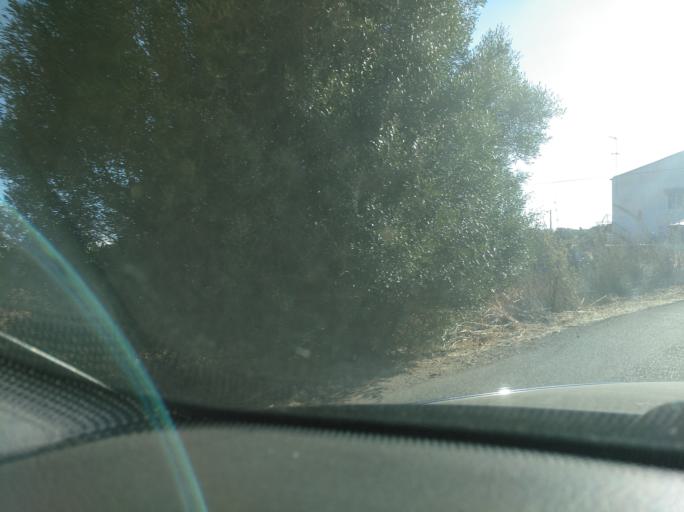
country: PT
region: Faro
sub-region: Vila Real de Santo Antonio
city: Monte Gordo
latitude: 37.1834
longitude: -7.5102
